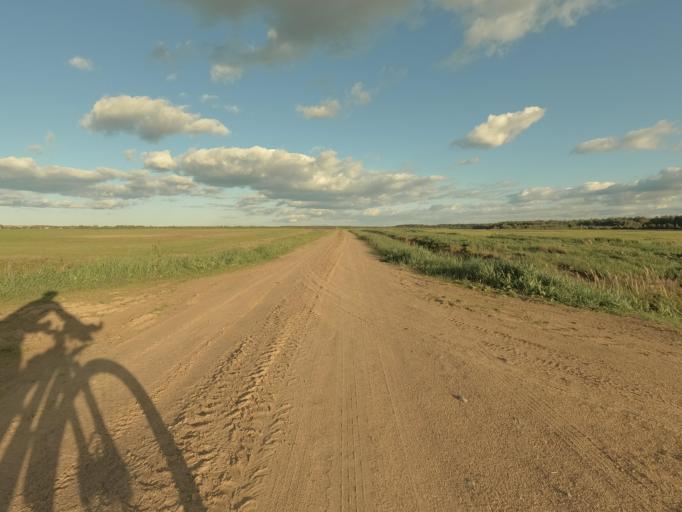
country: RU
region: Leningrad
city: Imeni Sverdlova
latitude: 59.8629
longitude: 30.7441
